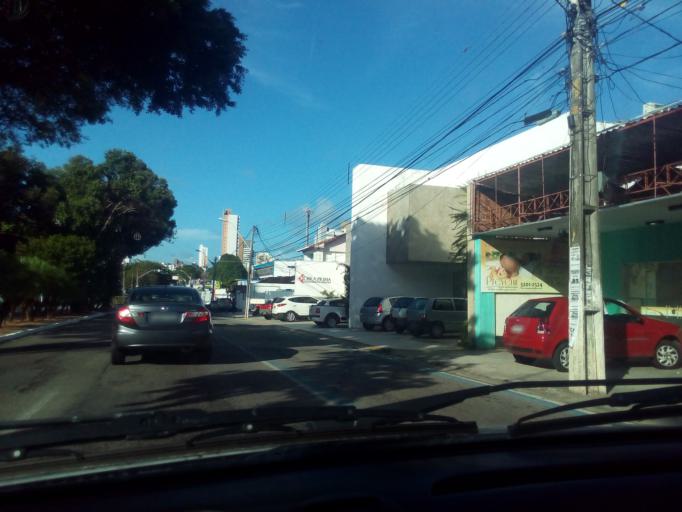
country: BR
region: Rio Grande do Norte
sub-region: Natal
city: Natal
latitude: -5.7979
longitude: -35.1996
